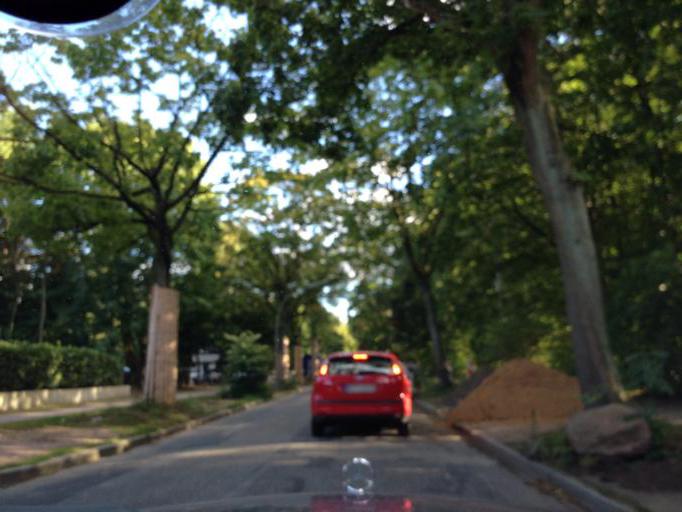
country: DE
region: Hamburg
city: Wandsbek
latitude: 53.5687
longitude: 10.0996
